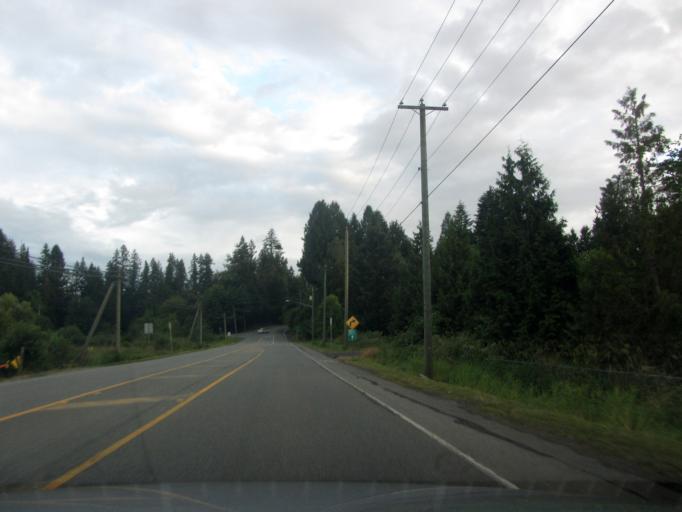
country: CA
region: British Columbia
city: Walnut Grove
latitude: 49.1548
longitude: -122.5910
